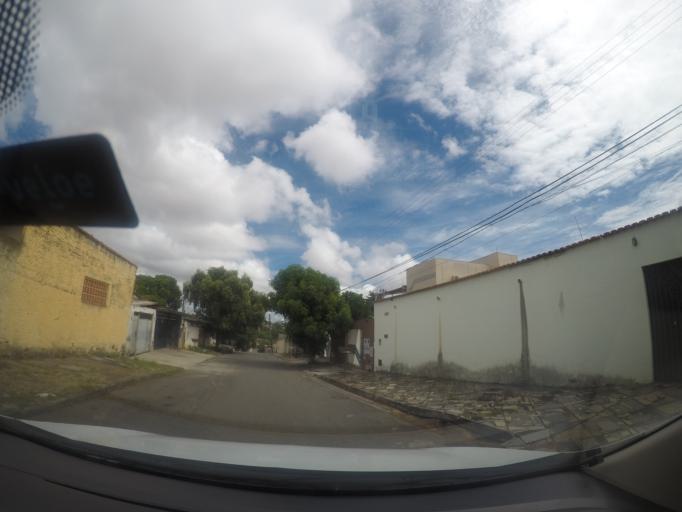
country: BR
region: Goias
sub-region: Goiania
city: Goiania
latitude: -16.6597
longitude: -49.3055
